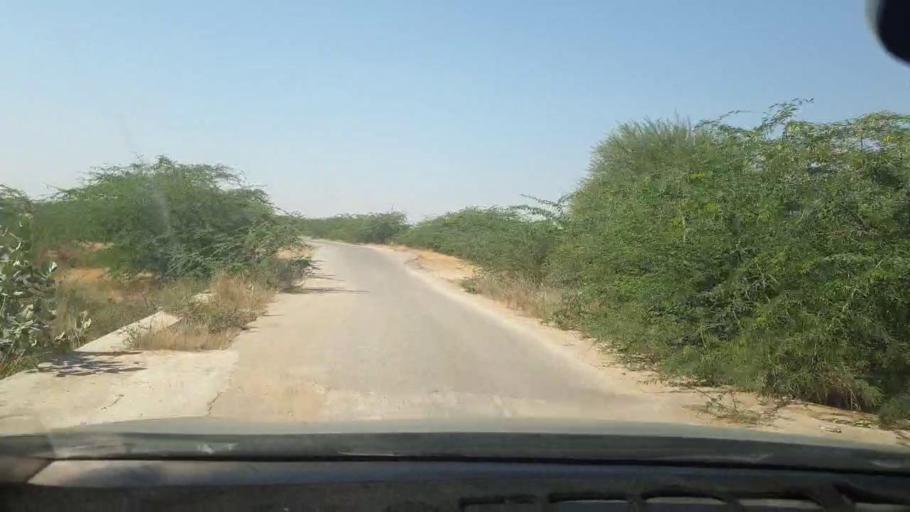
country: PK
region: Sindh
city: Malir Cantonment
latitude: 25.1621
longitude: 67.1598
